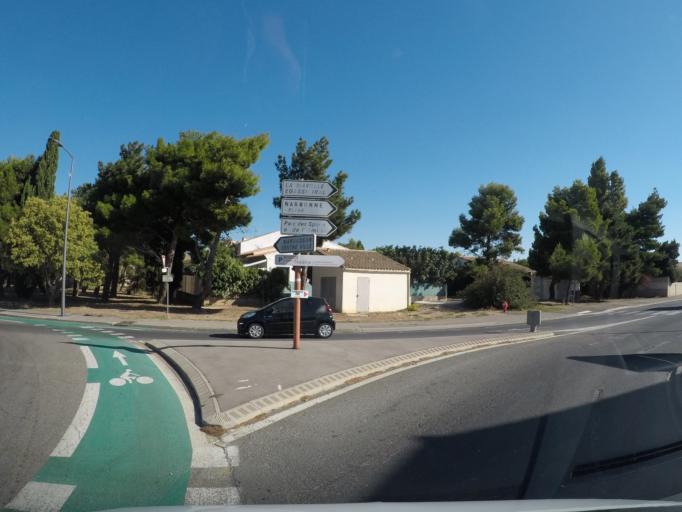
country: FR
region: Languedoc-Roussillon
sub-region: Departement de l'Aude
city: Narbonne
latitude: 43.1748
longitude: 3.0061
